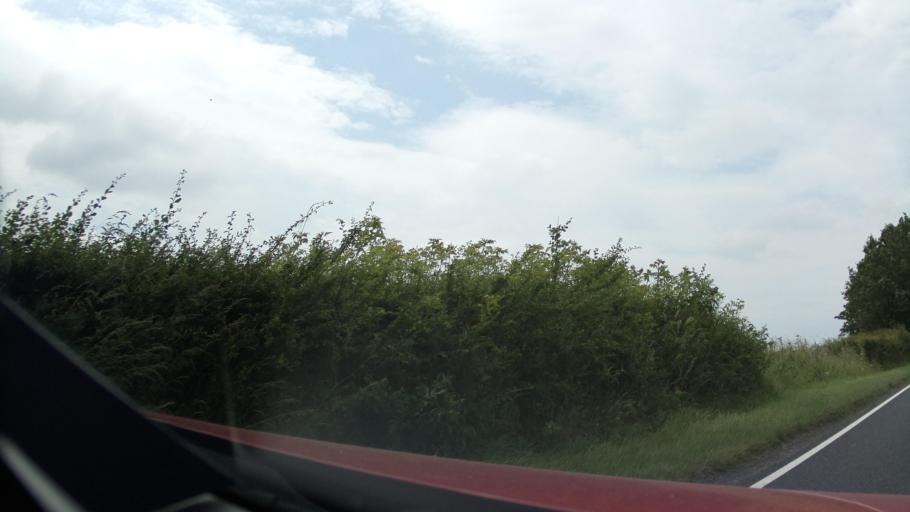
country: GB
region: Wales
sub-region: Vale of Glamorgan
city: Llantwit Major
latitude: 51.3967
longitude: -3.4262
